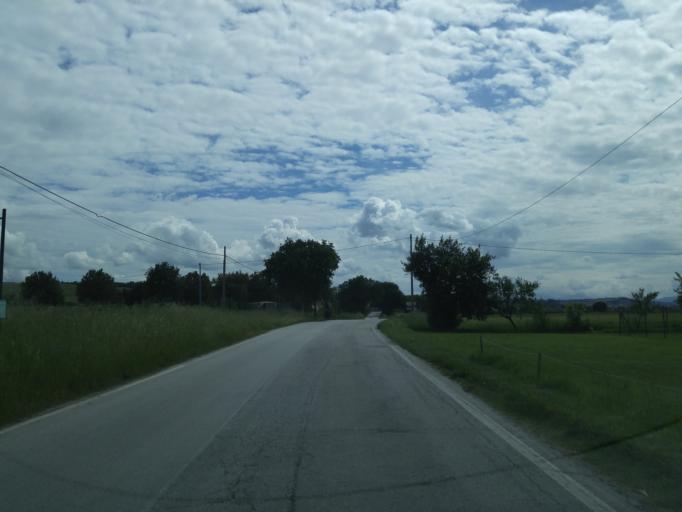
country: IT
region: The Marches
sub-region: Provincia di Pesaro e Urbino
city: Bellocchi
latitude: 43.8089
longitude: 13.0479
